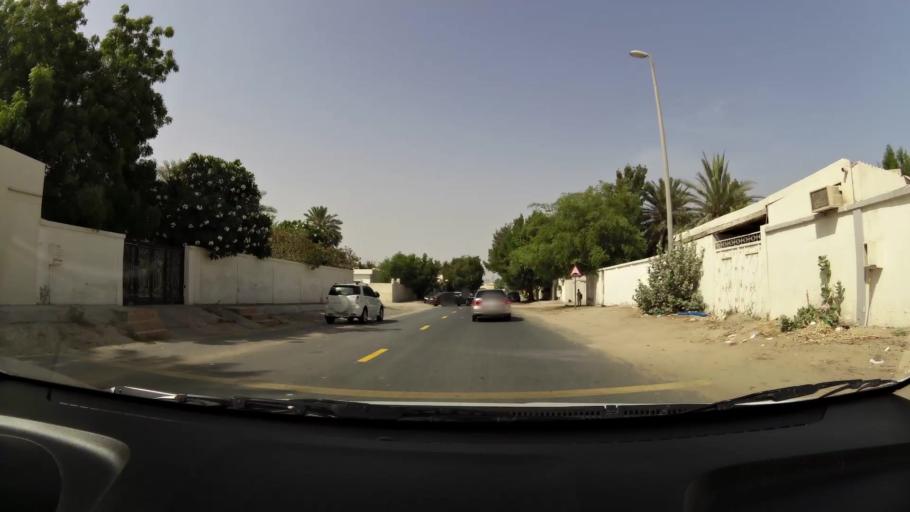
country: AE
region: Ash Shariqah
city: Sharjah
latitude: 25.3508
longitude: 55.4129
